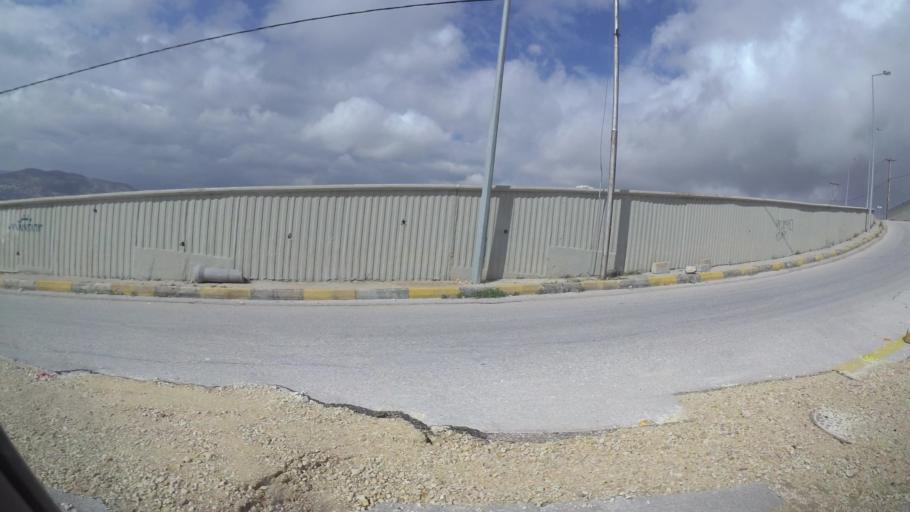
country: JO
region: Amman
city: Al Jubayhah
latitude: 32.0714
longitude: 35.8756
